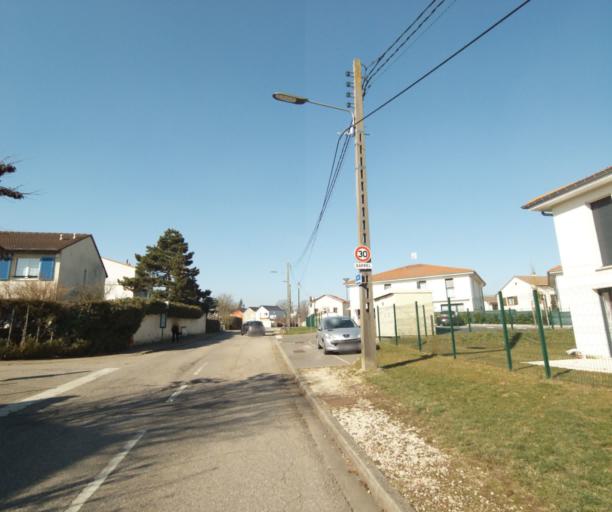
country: FR
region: Lorraine
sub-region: Departement de Meurthe-et-Moselle
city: Heillecourt
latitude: 48.6593
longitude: 6.1980
